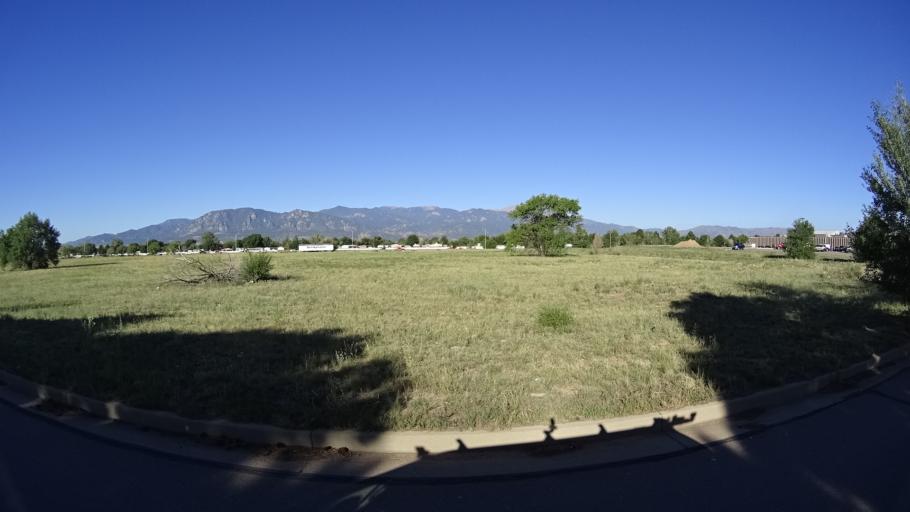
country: US
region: Colorado
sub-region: El Paso County
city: Security-Widefield
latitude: 38.7955
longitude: -104.7272
